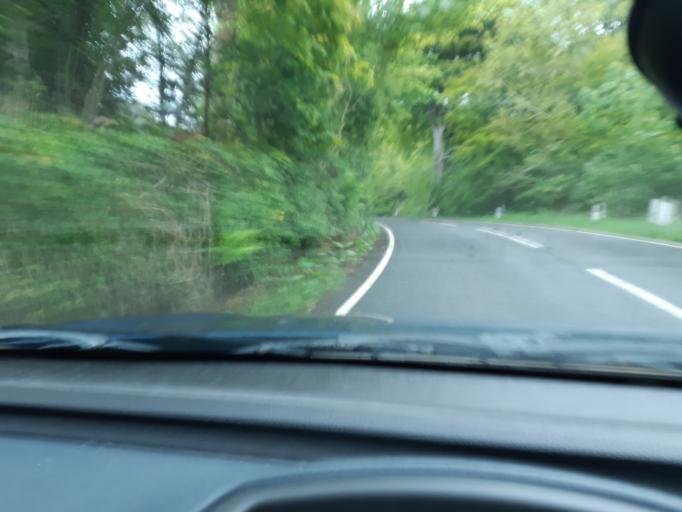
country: GB
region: Scotland
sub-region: Argyll and Bute
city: Oban
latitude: 56.2636
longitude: -5.4748
